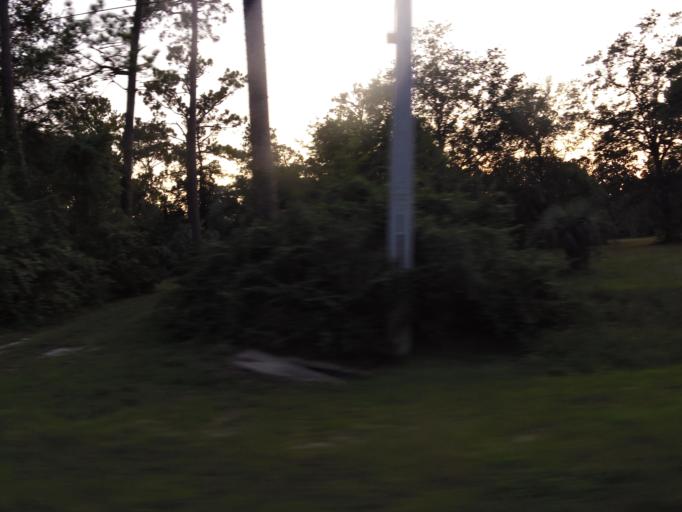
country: US
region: Florida
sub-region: Baker County
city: Macclenny
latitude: 30.2956
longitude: -82.1252
